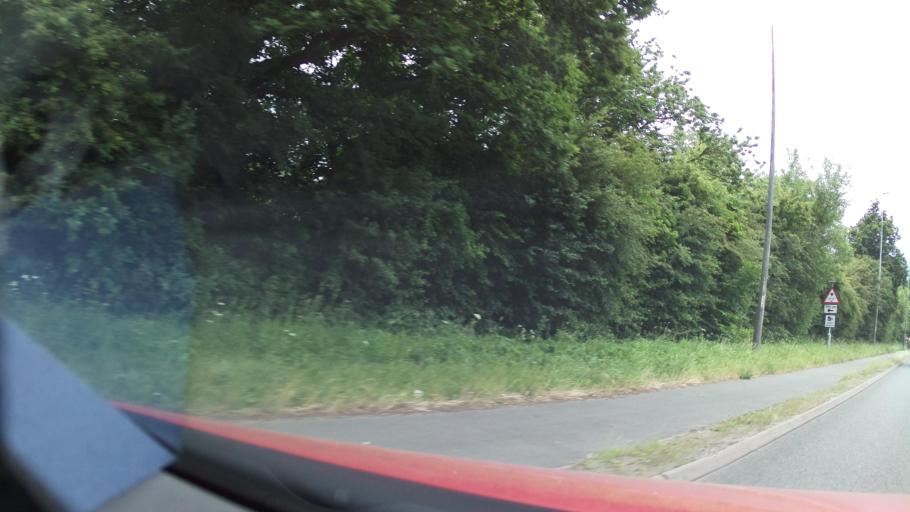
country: GB
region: England
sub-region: Staffordshire
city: Featherstone
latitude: 52.6473
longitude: -2.1280
